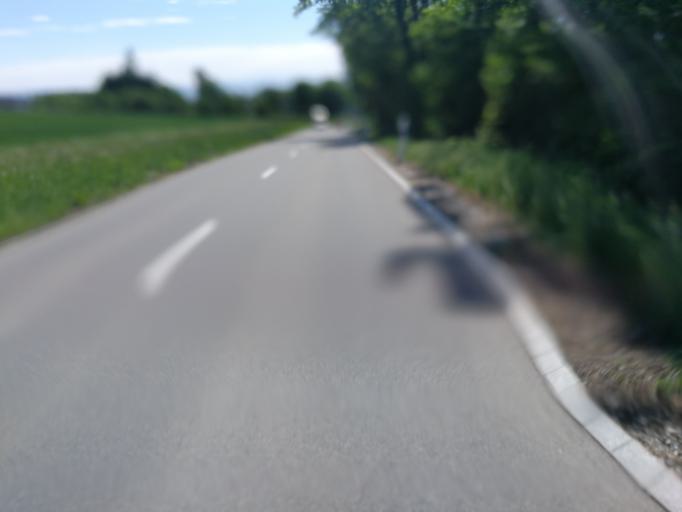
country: CH
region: Zurich
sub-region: Bezirk Meilen
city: Herrliberg
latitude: 47.3026
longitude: 8.6365
